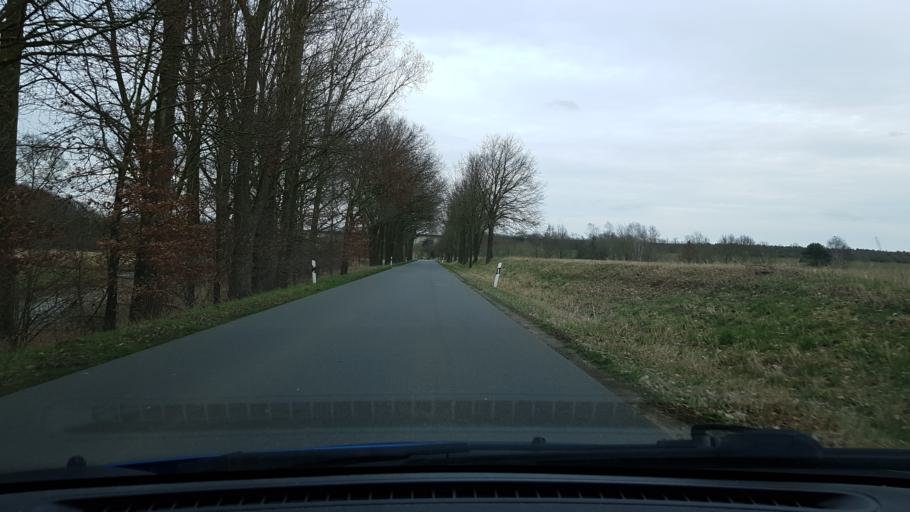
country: DE
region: Lower Saxony
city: Bad Bevensen
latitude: 53.0570
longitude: 10.5917
